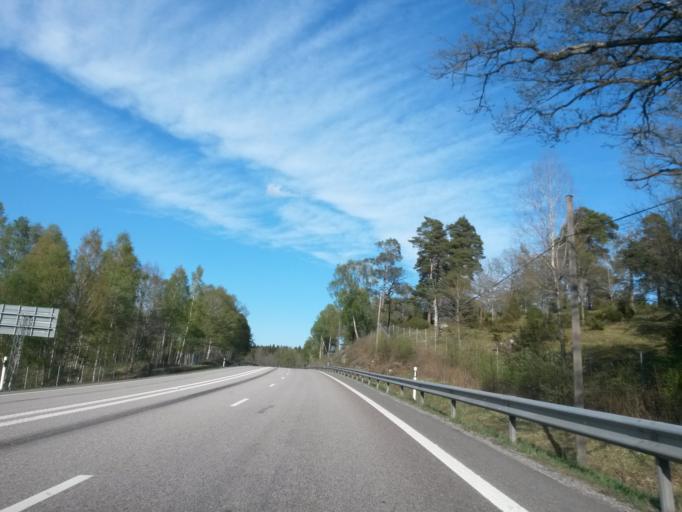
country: SE
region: Vaestra Goetaland
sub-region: Vargarda Kommun
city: Jonstorp
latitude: 58.0068
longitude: 12.7631
